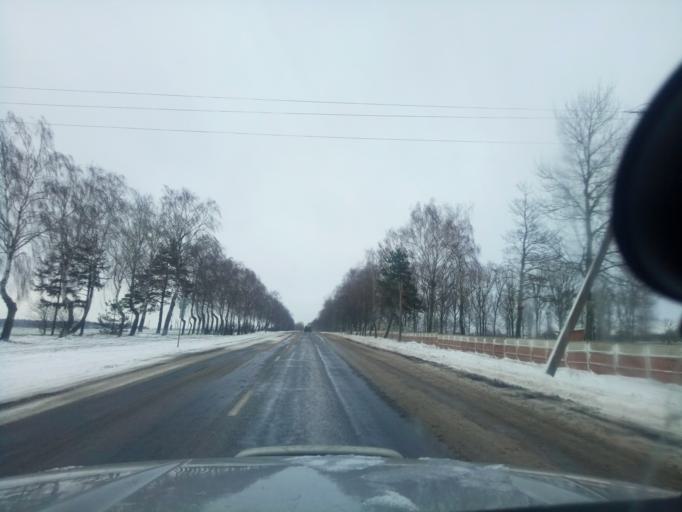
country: BY
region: Minsk
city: Tsimkavichy
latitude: 53.0867
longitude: 27.0200
